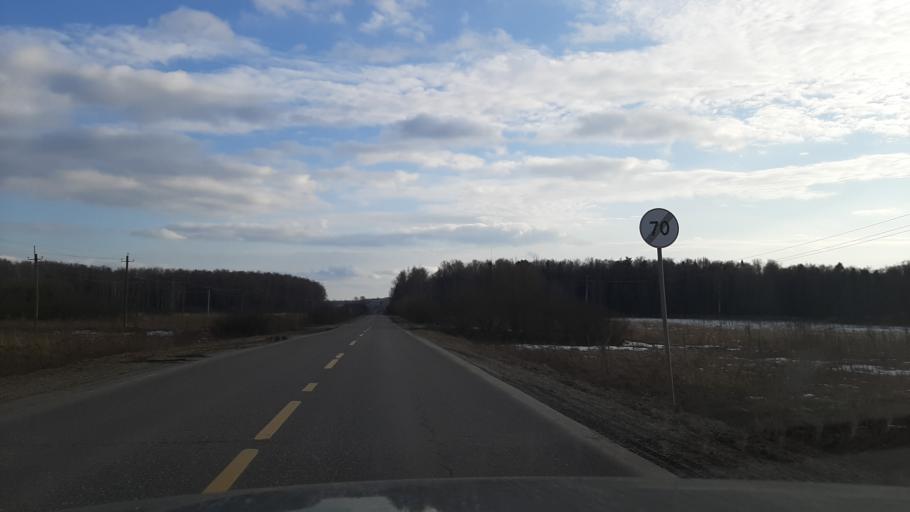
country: RU
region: Ivanovo
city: Novo-Talitsy
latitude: 56.9337
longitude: 40.7340
